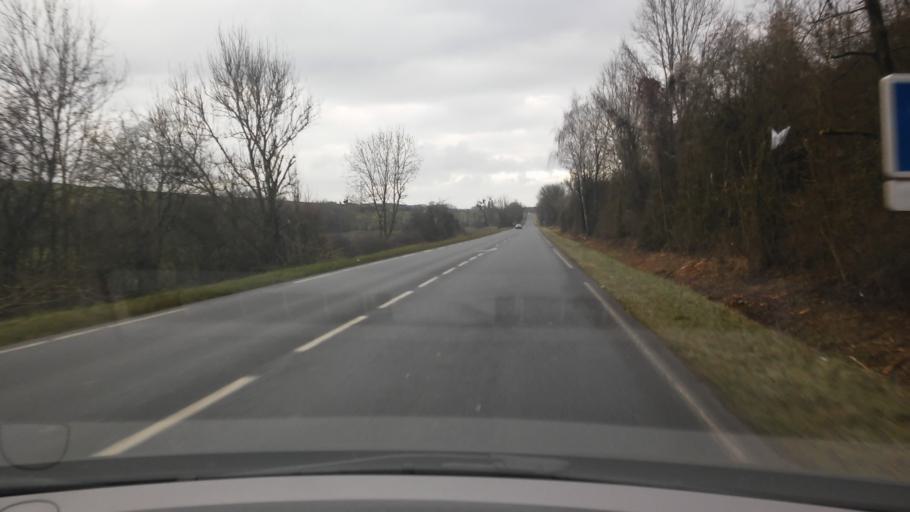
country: FR
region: Lorraine
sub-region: Departement de la Moselle
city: Courcelles-Chaussy
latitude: 49.1019
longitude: 6.4781
